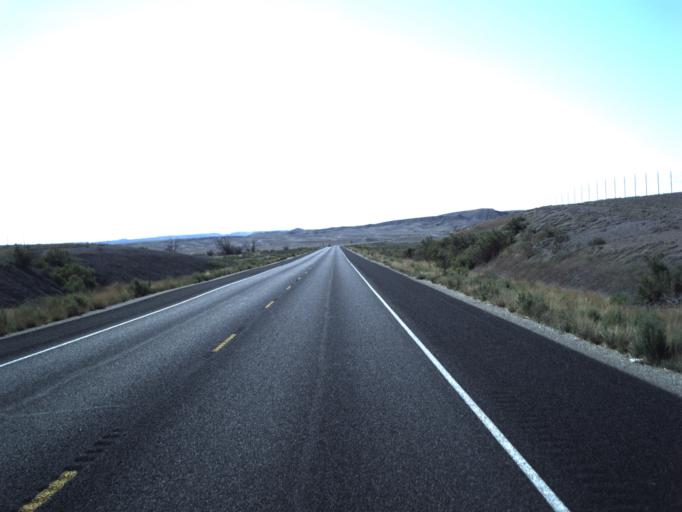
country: US
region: Utah
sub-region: Emery County
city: Ferron
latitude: 39.0585
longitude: -111.1280
